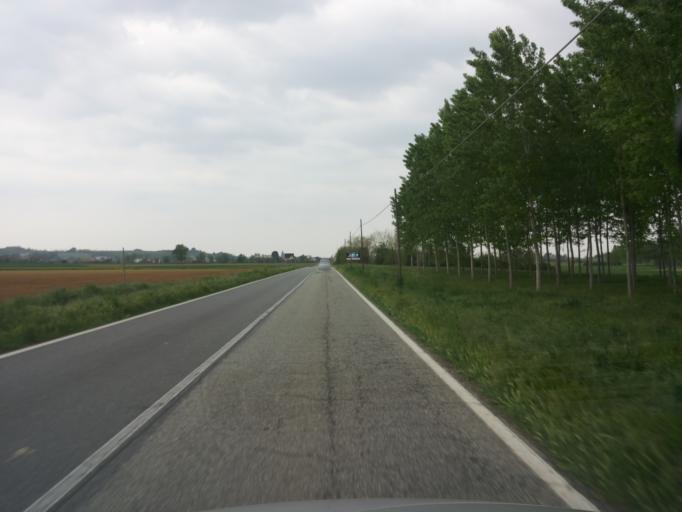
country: IT
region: Piedmont
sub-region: Provincia di Alessandria
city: Mirabello Monferrato
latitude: 45.0449
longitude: 8.5205
